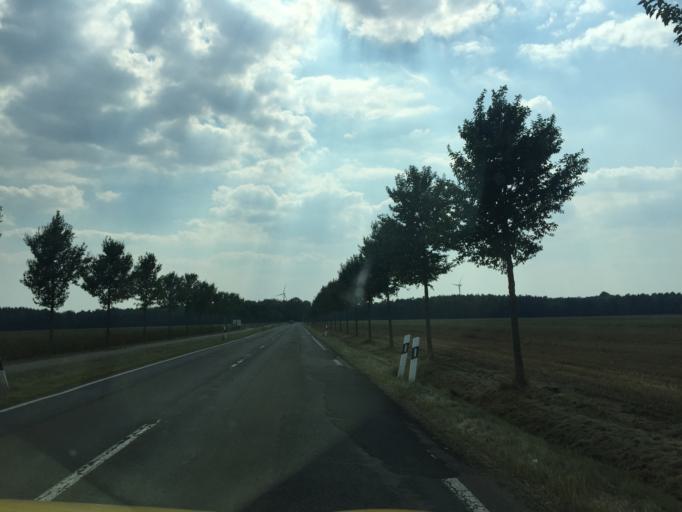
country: DE
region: Brandenburg
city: Welzow
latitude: 51.5687
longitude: 14.1788
